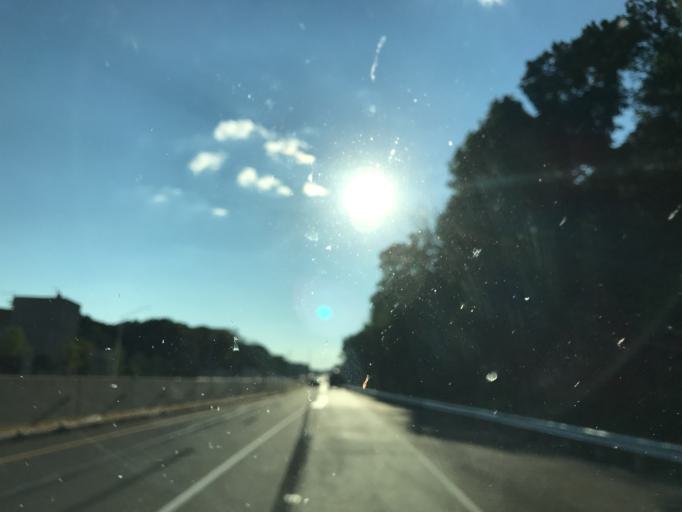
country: US
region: Pennsylvania
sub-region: Bucks County
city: Bristol
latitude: 40.1239
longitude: -74.8551
